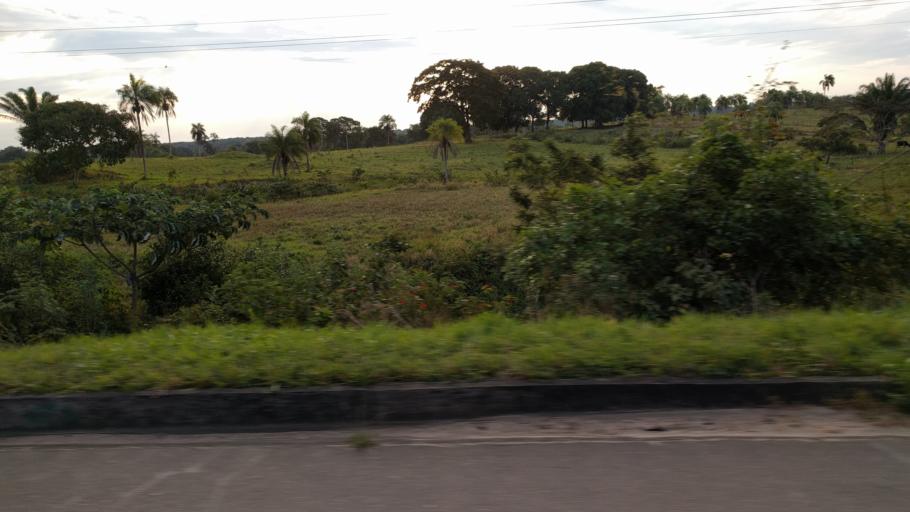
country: BO
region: Santa Cruz
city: Buena Vista
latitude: -17.4434
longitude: -63.6471
